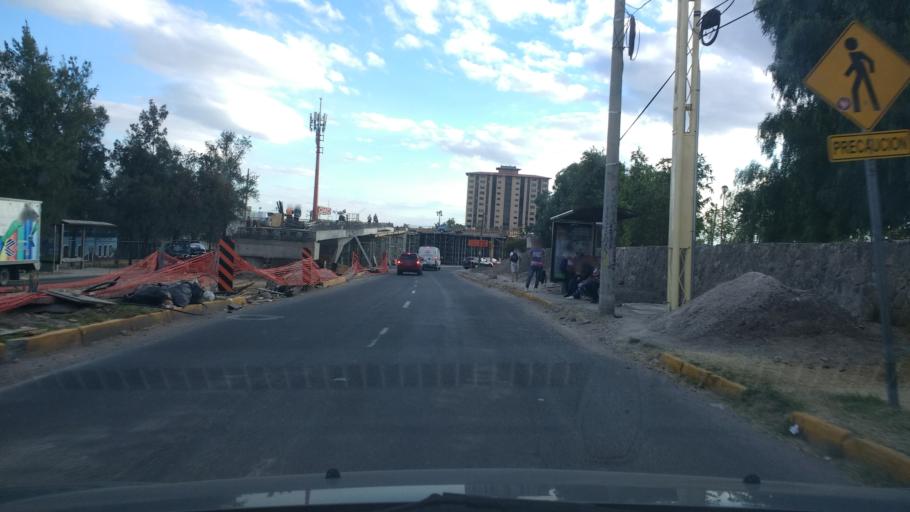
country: MX
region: Guanajuato
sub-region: Leon
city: La Ermita
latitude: 21.1716
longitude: -101.6983
